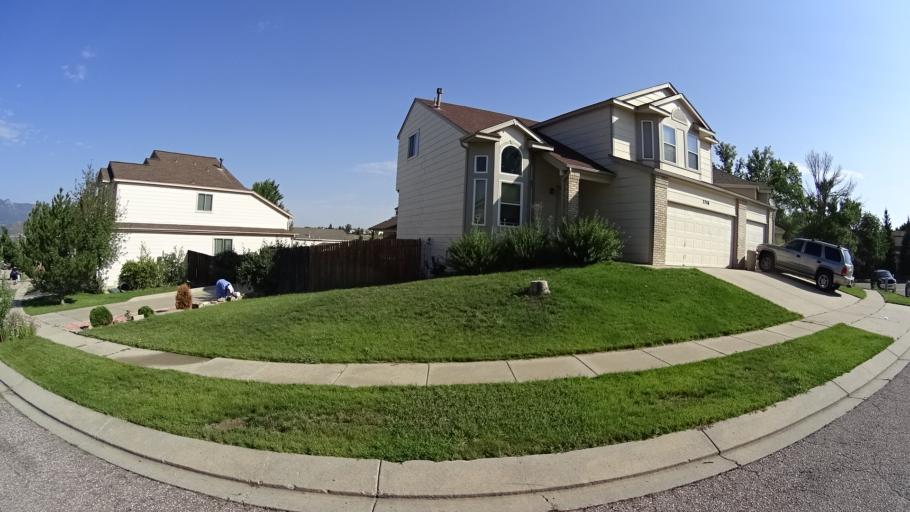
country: US
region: Colorado
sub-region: El Paso County
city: Air Force Academy
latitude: 38.9465
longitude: -104.7770
